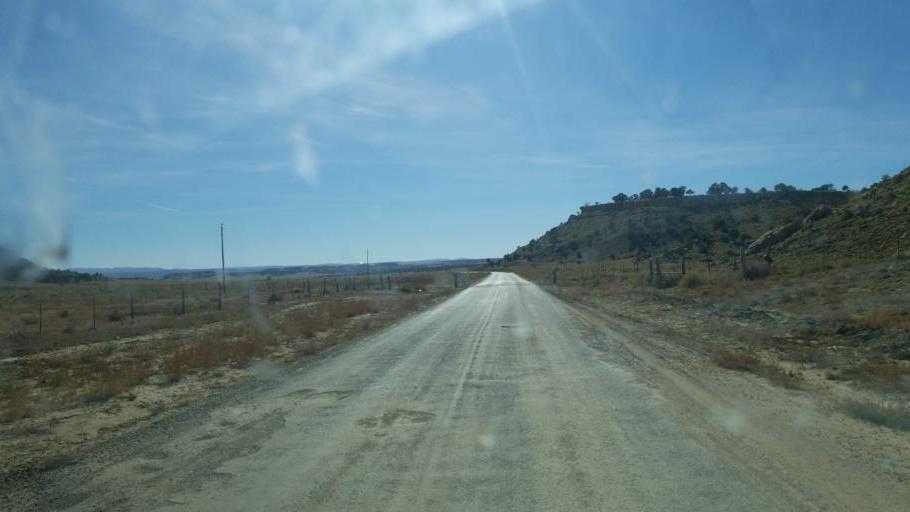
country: US
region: New Mexico
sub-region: McKinley County
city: Thoreau
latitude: 35.4882
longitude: -108.0343
